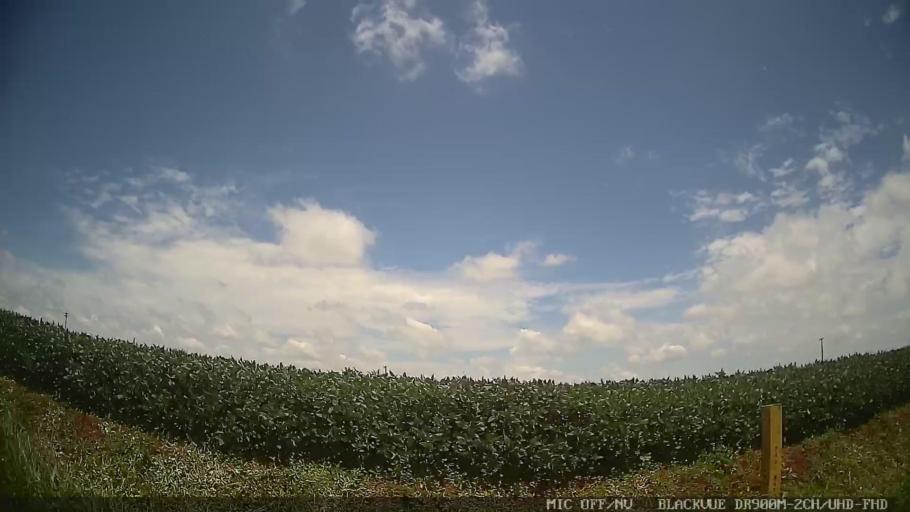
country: BR
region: Sao Paulo
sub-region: Laranjal Paulista
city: Laranjal Paulista
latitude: -23.0290
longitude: -47.8576
